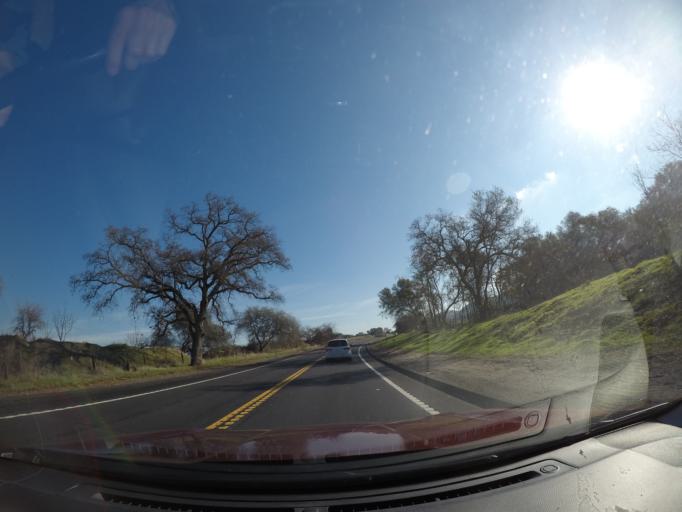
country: US
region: California
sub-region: Stanislaus County
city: East Oakdale
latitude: 37.8061
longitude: -120.6868
